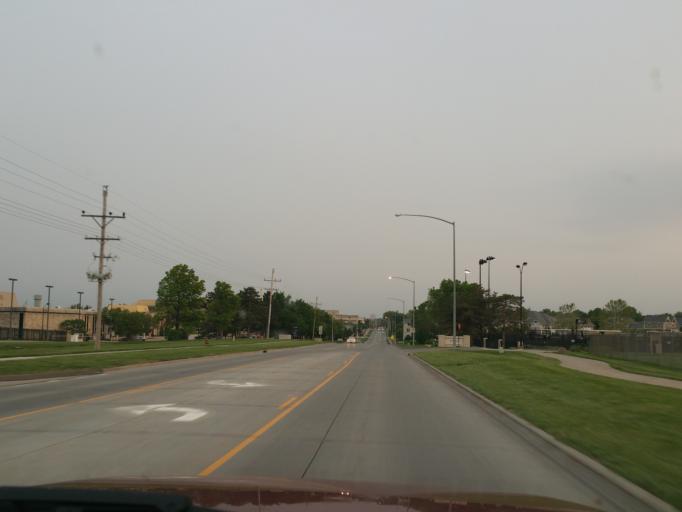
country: US
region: Kansas
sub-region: Riley County
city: Manhattan
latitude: 39.2018
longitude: -96.5857
